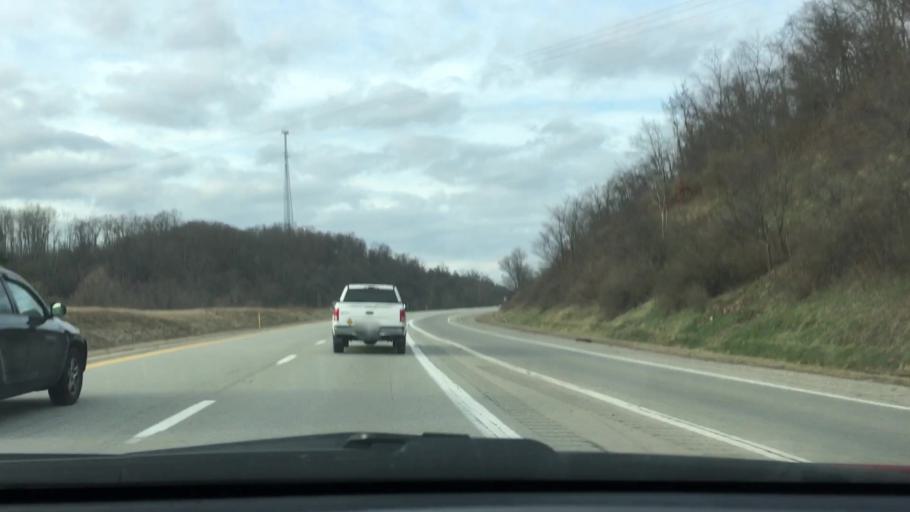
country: US
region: Pennsylvania
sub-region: Greene County
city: Waynesburg
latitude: 39.9588
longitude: -80.1710
